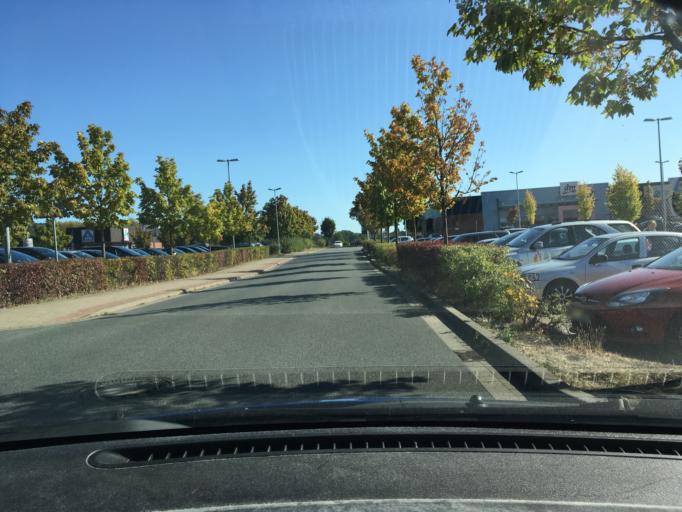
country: DE
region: Lower Saxony
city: Springe
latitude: 52.2120
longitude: 9.5693
